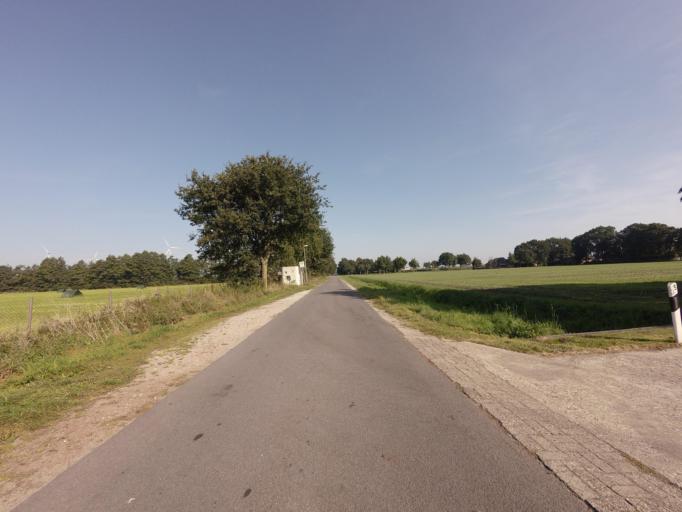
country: DE
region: Lower Saxony
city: Laar
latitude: 52.5730
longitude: 6.7804
